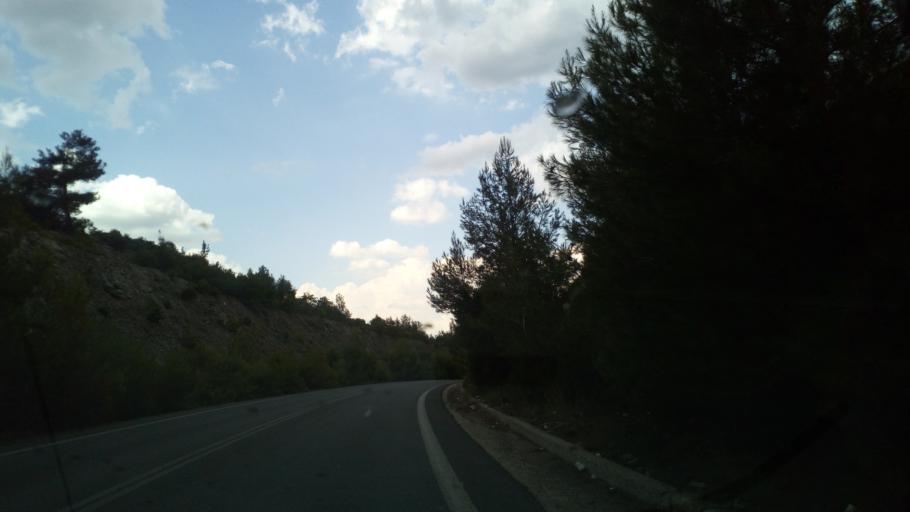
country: GR
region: Central Macedonia
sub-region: Nomos Chalkidikis
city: Polygyros
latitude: 40.3585
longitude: 23.4390
